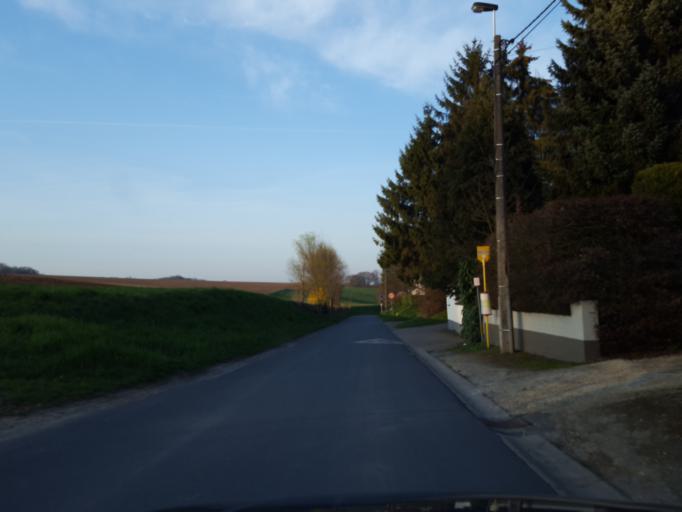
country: BE
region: Wallonia
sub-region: Province du Brabant Wallon
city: Louvain-la-Neuve
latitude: 50.6739
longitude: 4.6337
